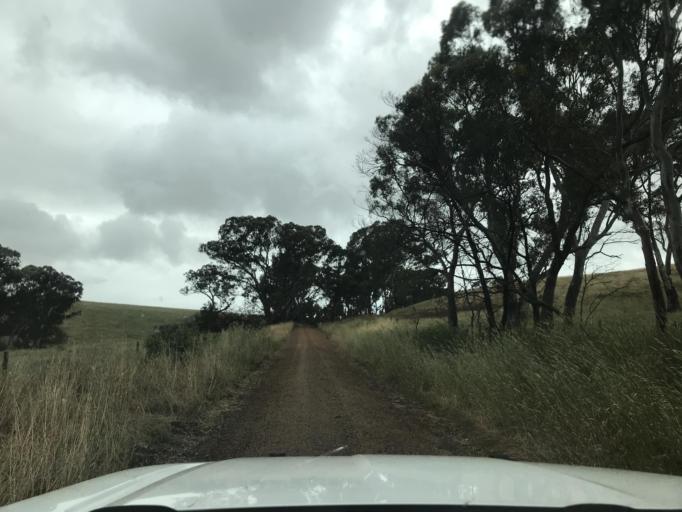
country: AU
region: South Australia
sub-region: Wattle Range
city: Penola
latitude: -37.2346
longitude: 141.4673
